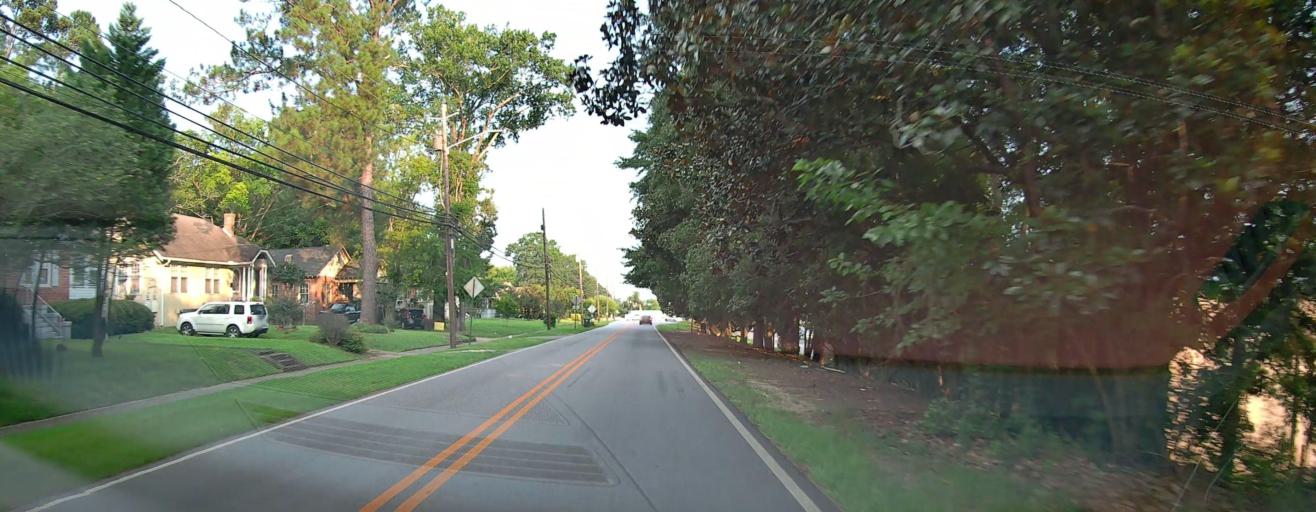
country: US
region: Georgia
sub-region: Bibb County
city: Macon
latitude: 32.8515
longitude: -83.6260
